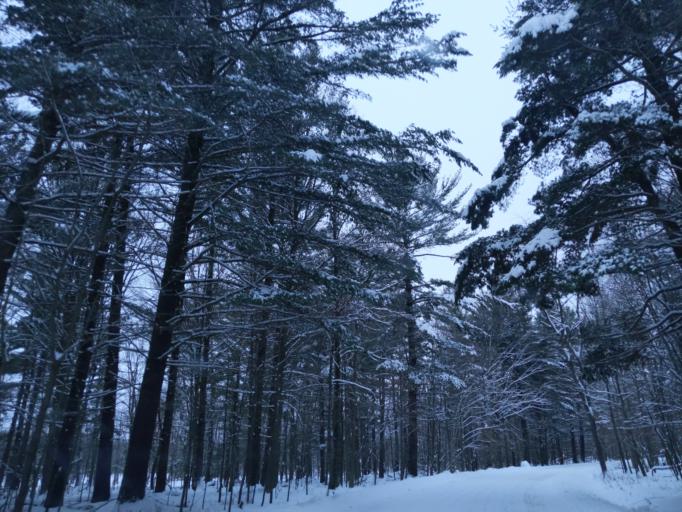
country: US
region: Wisconsin
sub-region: Marathon County
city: Mosinee
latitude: 44.7626
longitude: -89.8694
